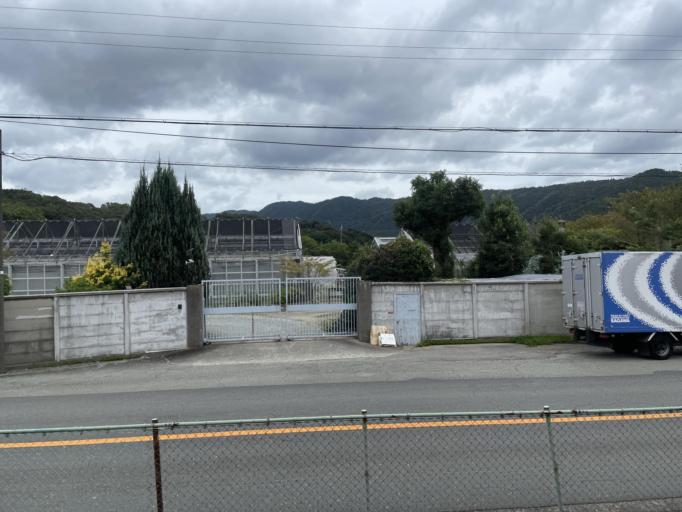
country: JP
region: Osaka
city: Ikeda
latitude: 34.8467
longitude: 135.4197
